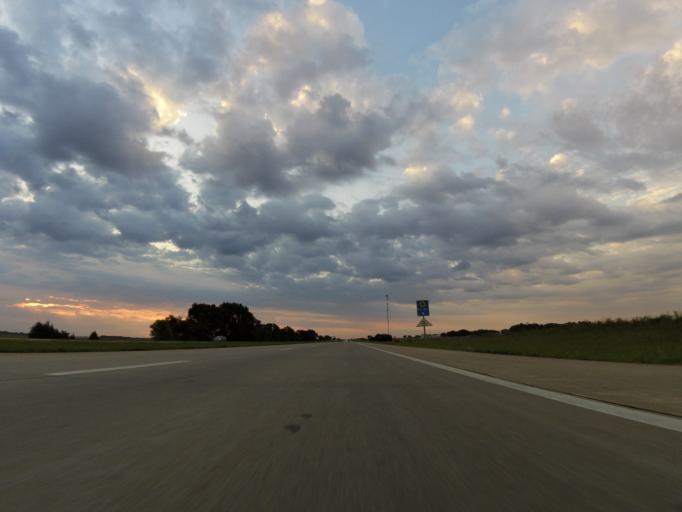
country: US
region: Kansas
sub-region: Reno County
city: Haven
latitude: 37.9141
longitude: -97.8176
